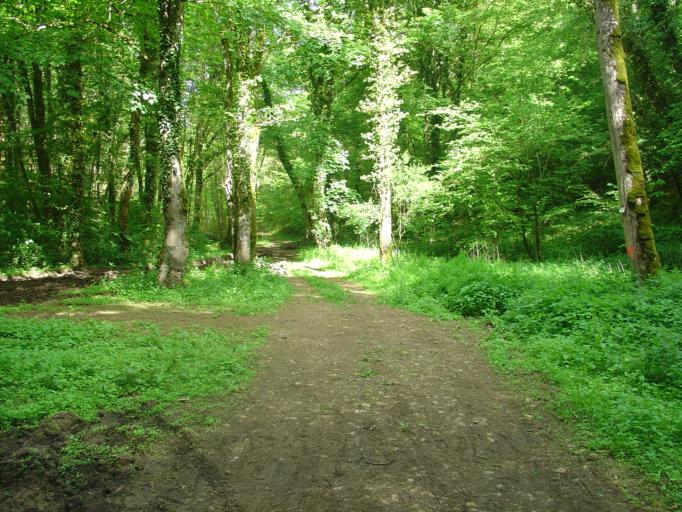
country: FR
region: Lorraine
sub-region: Departement de Meurthe-et-Moselle
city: Montauville
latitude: 48.8563
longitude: 5.9289
